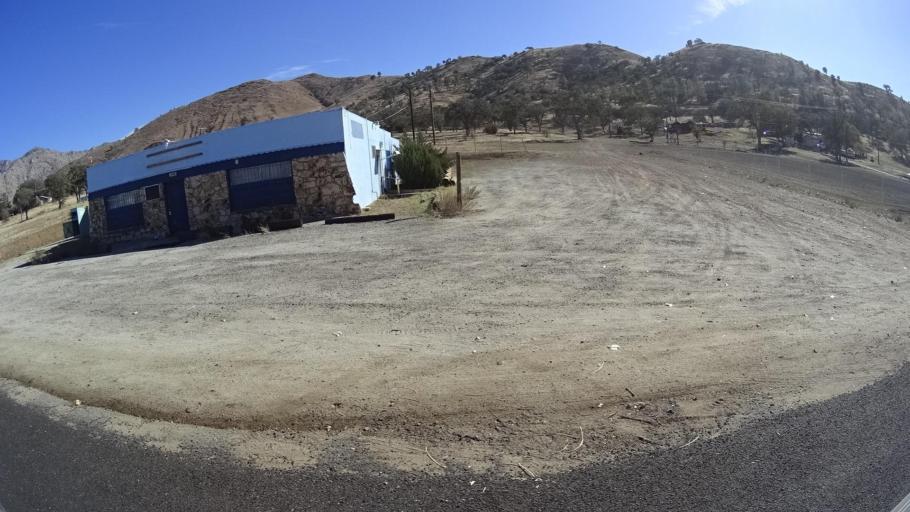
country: US
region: California
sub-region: Kern County
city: Bodfish
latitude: 35.5999
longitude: -118.4886
